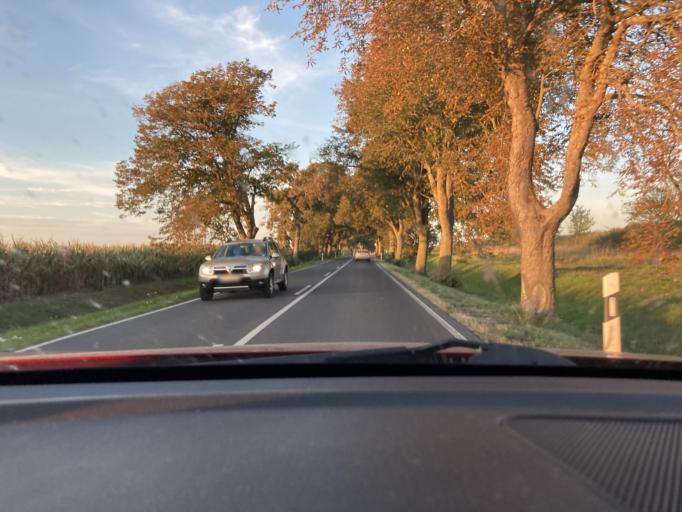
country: DE
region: Mecklenburg-Vorpommern
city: Alt-Sanitz
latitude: 53.7692
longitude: 13.6491
